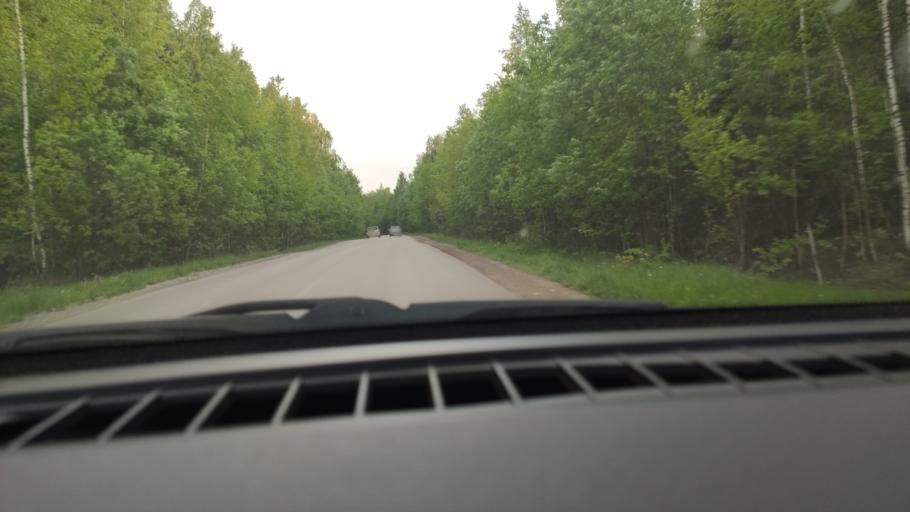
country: RU
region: Perm
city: Kondratovo
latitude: 58.0649
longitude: 56.0022
